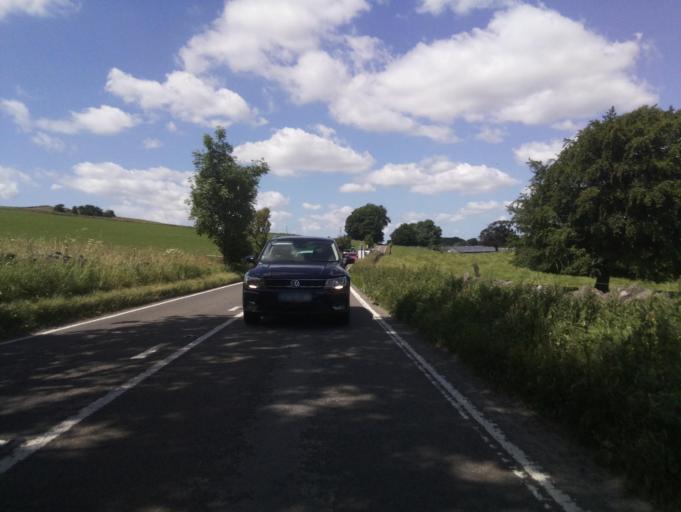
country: GB
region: England
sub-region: Derbyshire
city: Ashbourne
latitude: 53.0850
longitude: -1.7627
